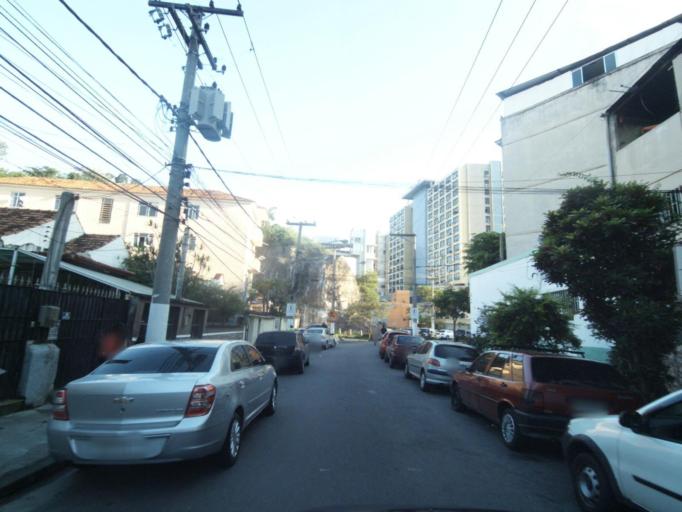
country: BR
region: Rio de Janeiro
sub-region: Niteroi
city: Niteroi
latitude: -22.8911
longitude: -43.1178
